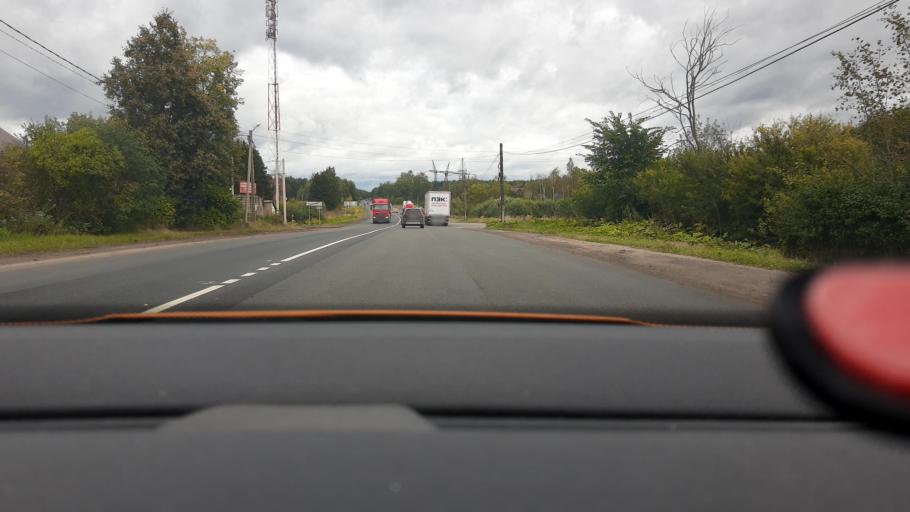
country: RU
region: Moskovskaya
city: Lesnoy
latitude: 56.0523
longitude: 37.9954
